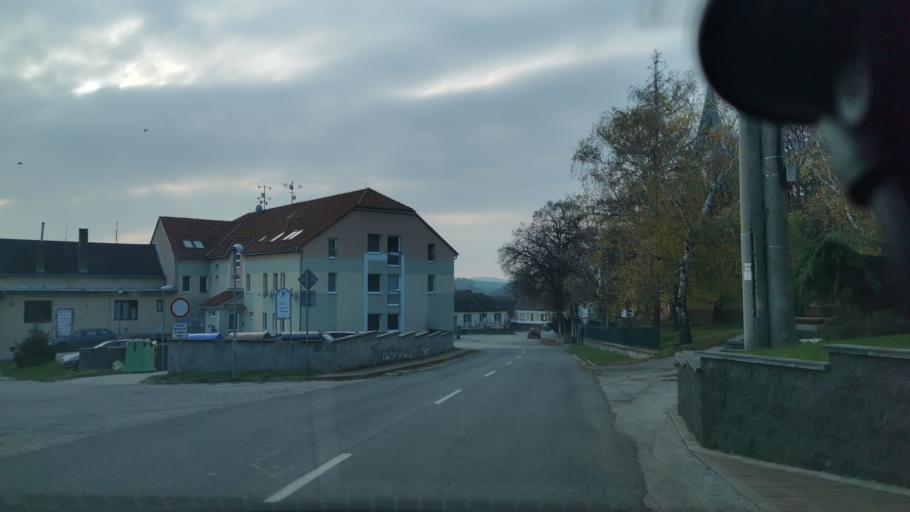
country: SK
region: Trnavsky
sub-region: Okres Skalica
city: Skalica
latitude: 48.7728
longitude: 17.2816
